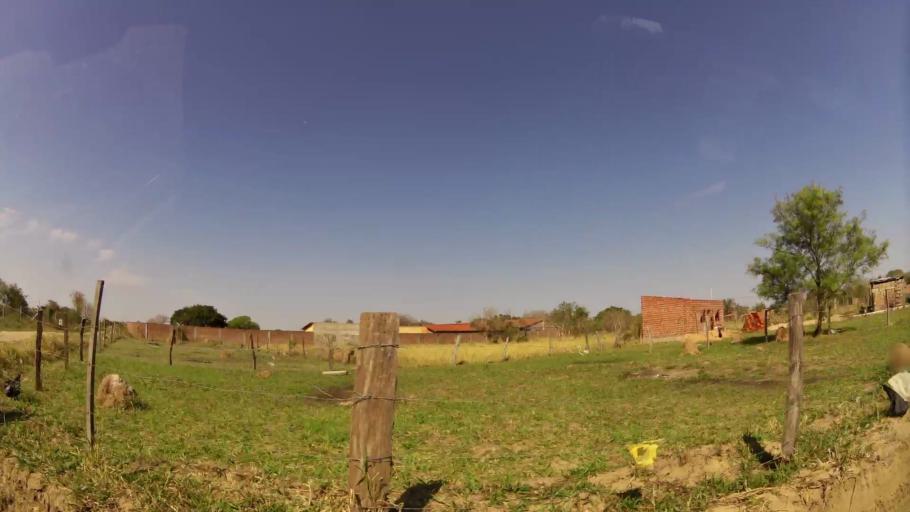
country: BO
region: Santa Cruz
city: Cotoca
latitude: -17.7335
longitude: -63.0737
